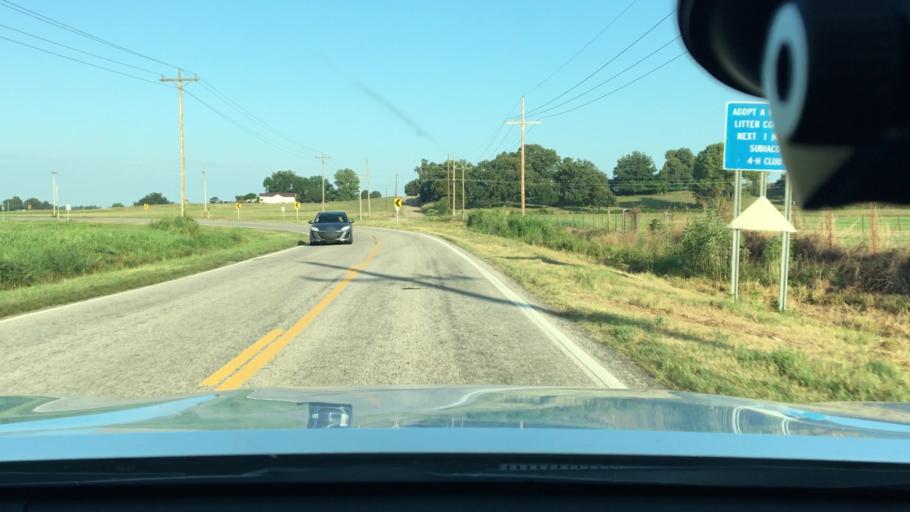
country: US
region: Arkansas
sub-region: Johnson County
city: Coal Hill
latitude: 35.3377
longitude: -93.6295
